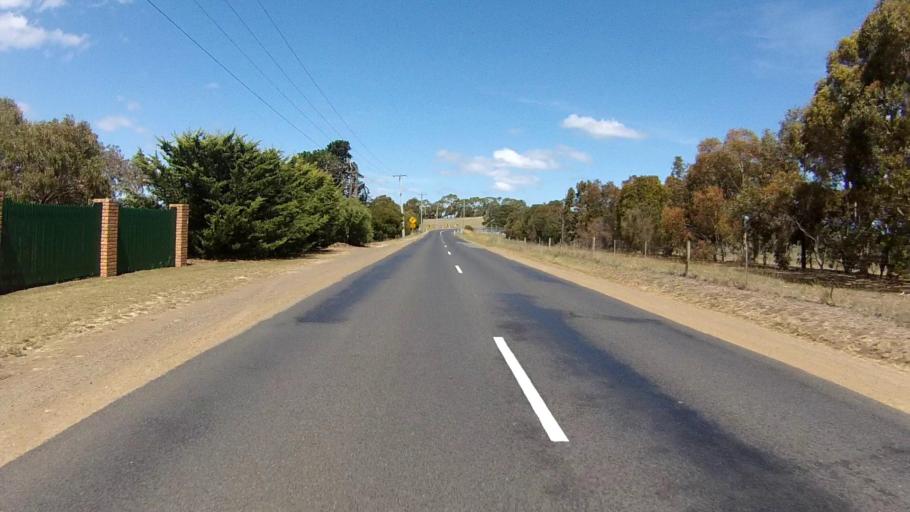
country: AU
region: Tasmania
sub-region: Sorell
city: Sorell
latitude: -42.7799
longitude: 147.5228
